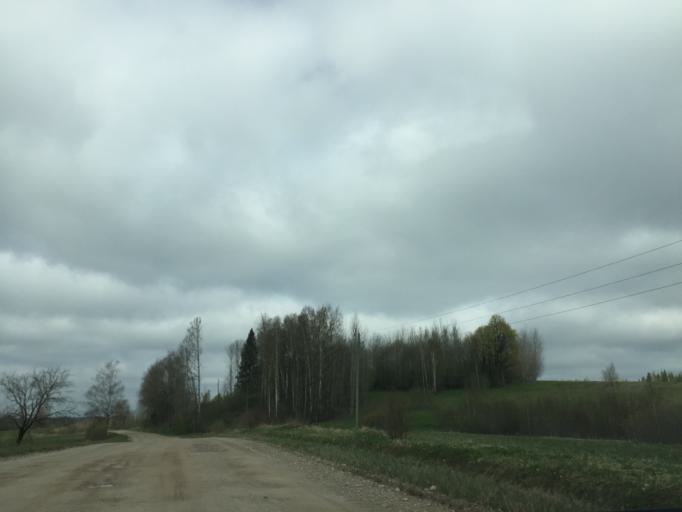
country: EE
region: Valgamaa
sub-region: Valga linn
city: Valga
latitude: 57.5620
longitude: 26.2743
